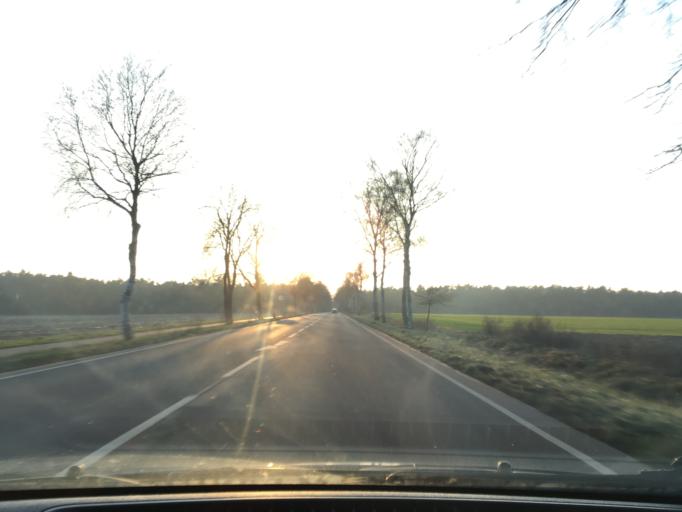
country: DE
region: Lower Saxony
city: Eschede
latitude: 52.7256
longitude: 10.2221
